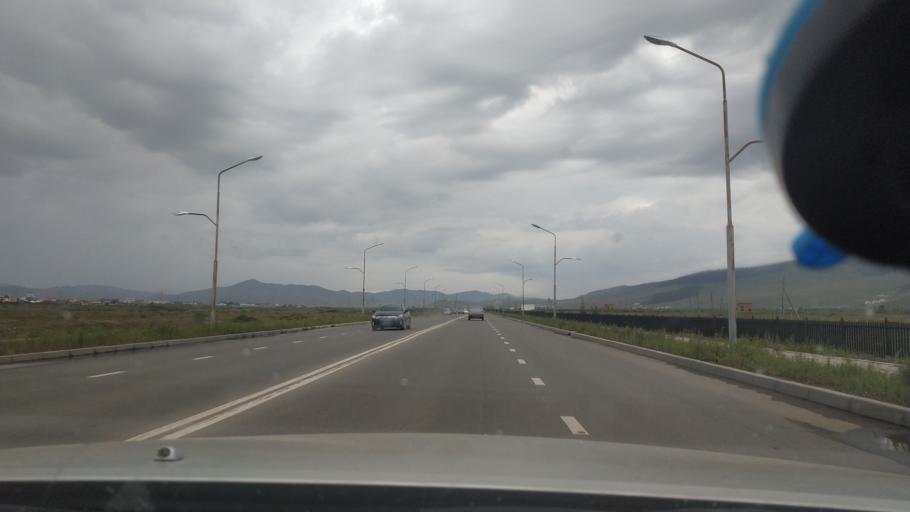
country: MN
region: Ulaanbaatar
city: Ulaanbaatar
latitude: 47.9026
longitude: 106.9821
